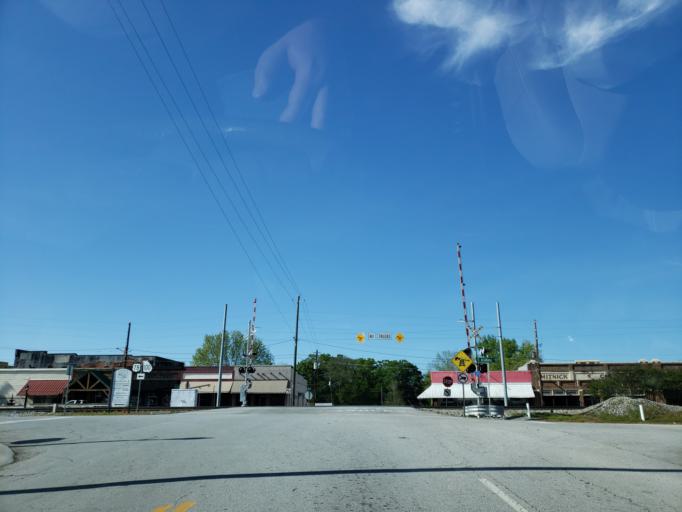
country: US
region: Georgia
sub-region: Haralson County
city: Tallapoosa
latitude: 33.7438
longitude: -85.2874
